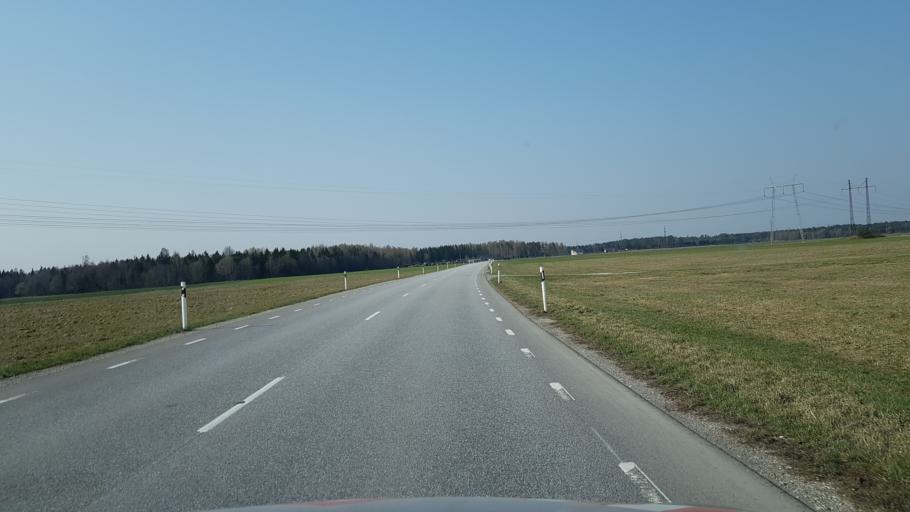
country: EE
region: Harju
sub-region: Saku vald
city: Saku
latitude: 59.2640
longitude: 24.7204
